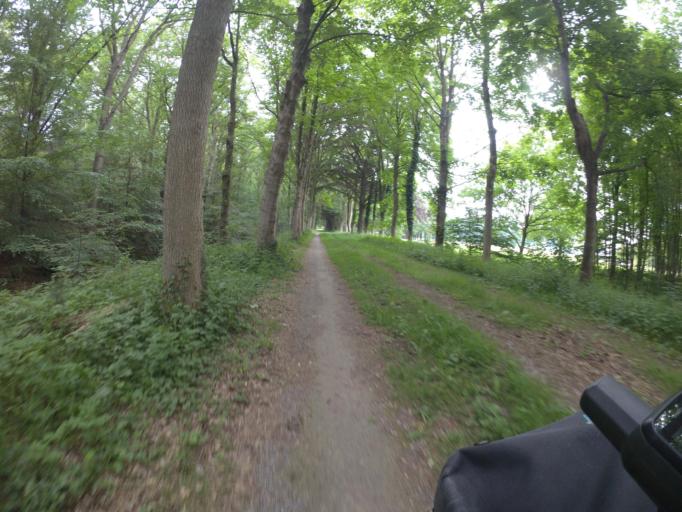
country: NL
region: Groningen
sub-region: Gemeente Leek
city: Leek
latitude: 53.0196
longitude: 6.4136
